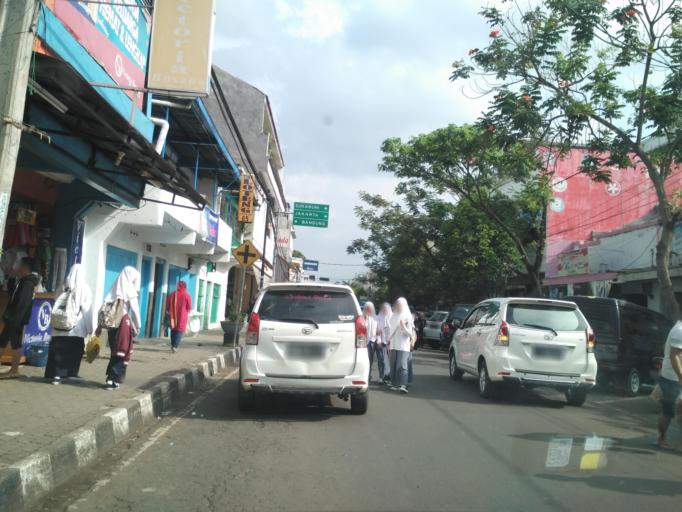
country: ID
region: West Java
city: Ciranjang-hilir
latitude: -6.8214
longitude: 107.1418
